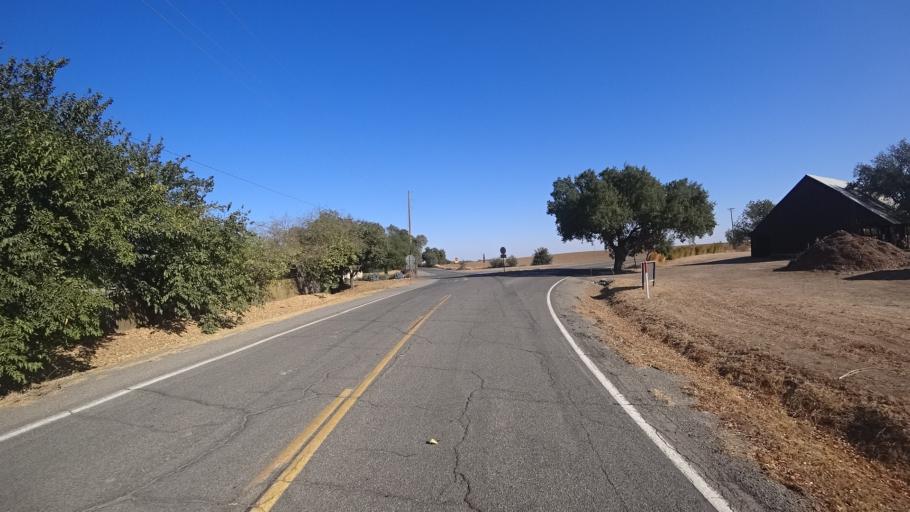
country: US
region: California
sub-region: Yolo County
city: Woodland
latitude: 38.6775
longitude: -121.8688
